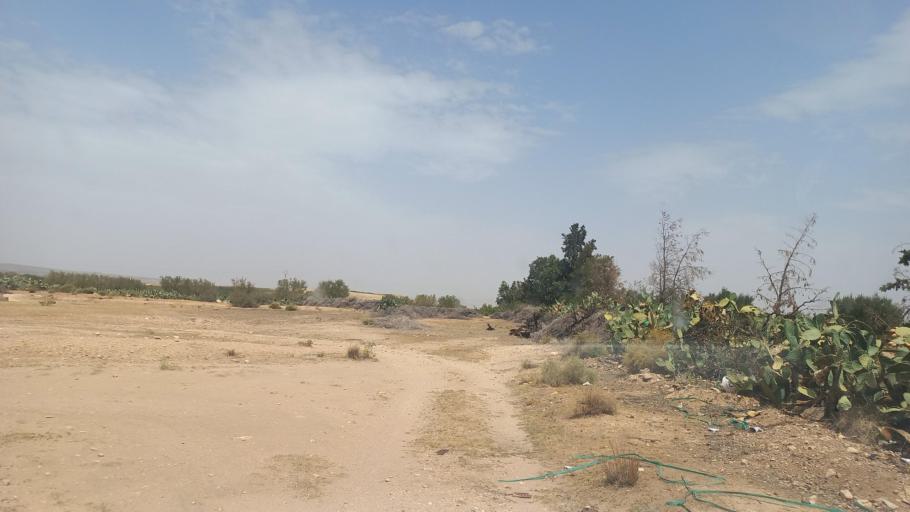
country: TN
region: Al Qasrayn
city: Kasserine
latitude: 35.2637
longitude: 8.9867
